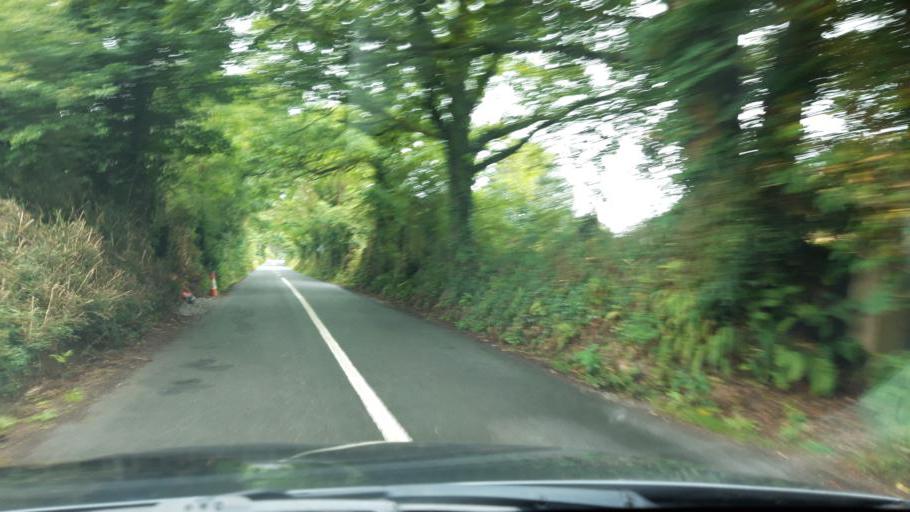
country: IE
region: Munster
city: Cahir
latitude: 52.1737
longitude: -7.8674
